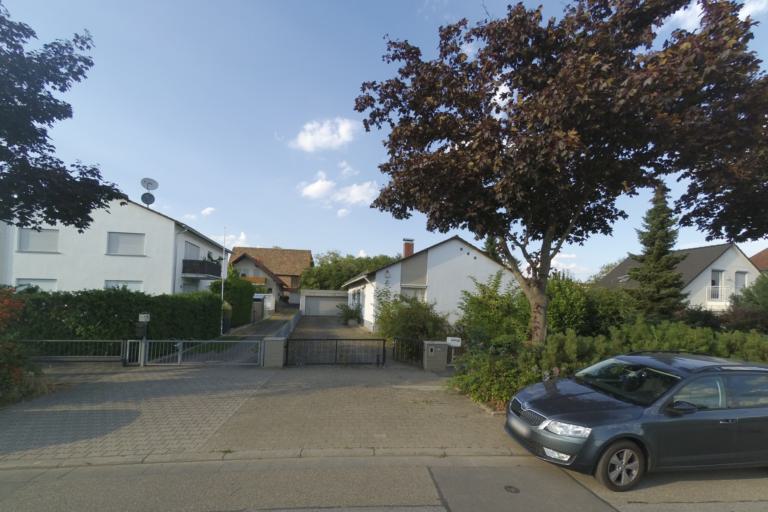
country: DE
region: Hesse
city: Lampertheim
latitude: 49.5911
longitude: 8.4706
